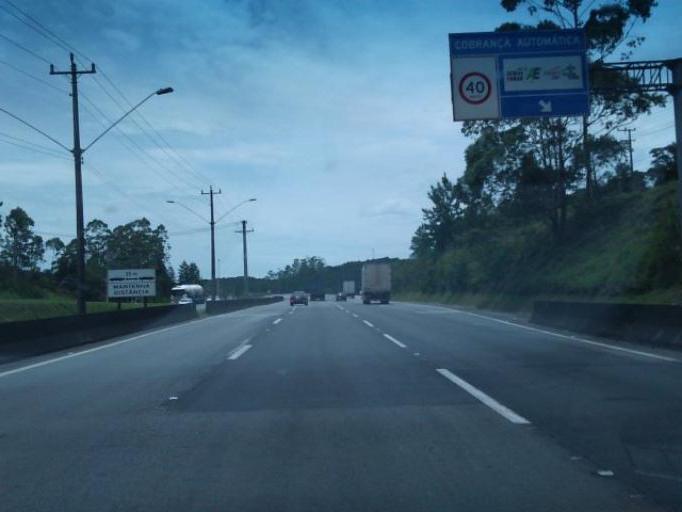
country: BR
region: Sao Paulo
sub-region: Sao Lourenco Da Serra
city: Sao Lourenco da Serra
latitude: -23.7833
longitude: -46.9146
